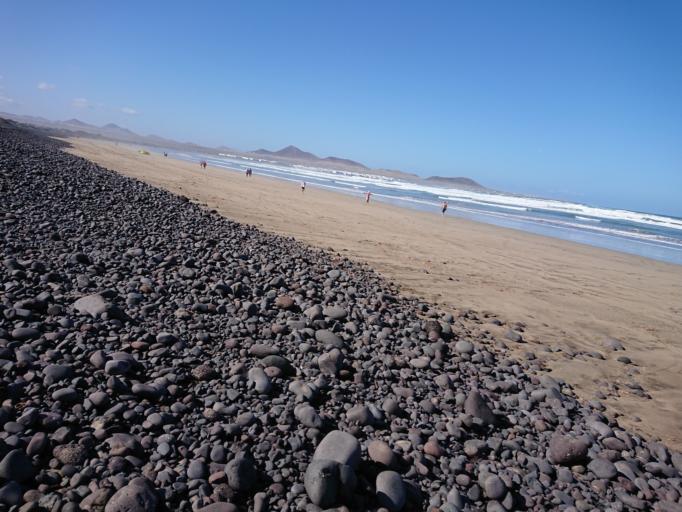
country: ES
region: Canary Islands
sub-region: Provincia de Las Palmas
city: Haria
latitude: 29.1207
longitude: -13.5436
